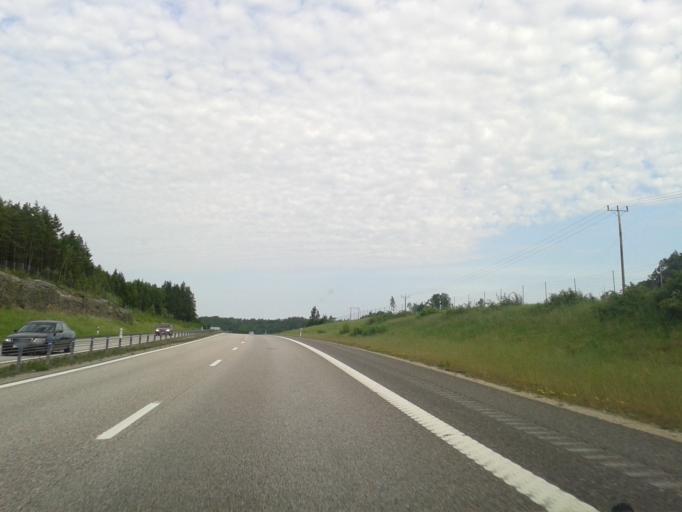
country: SE
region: Vaestra Goetaland
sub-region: Munkedals Kommun
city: Munkedal
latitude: 58.4741
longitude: 11.6442
